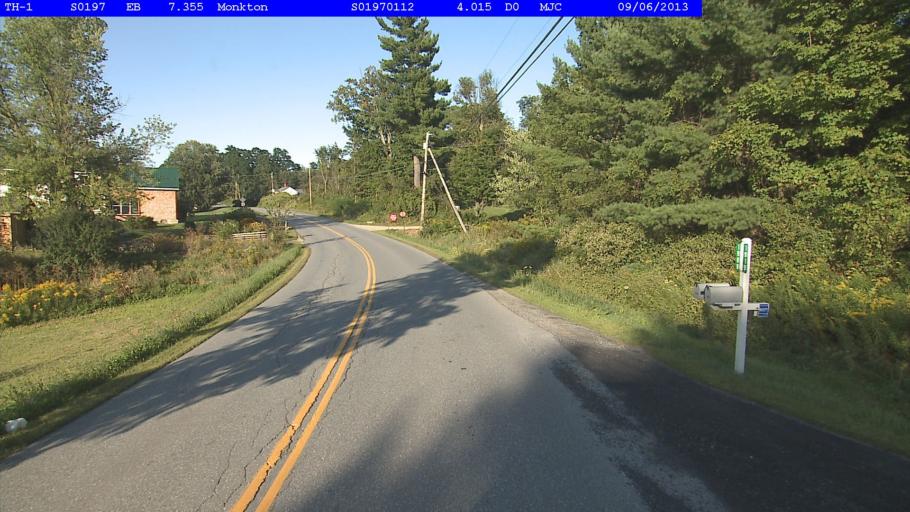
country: US
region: Vermont
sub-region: Chittenden County
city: Hinesburg
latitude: 44.2335
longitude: -73.1481
